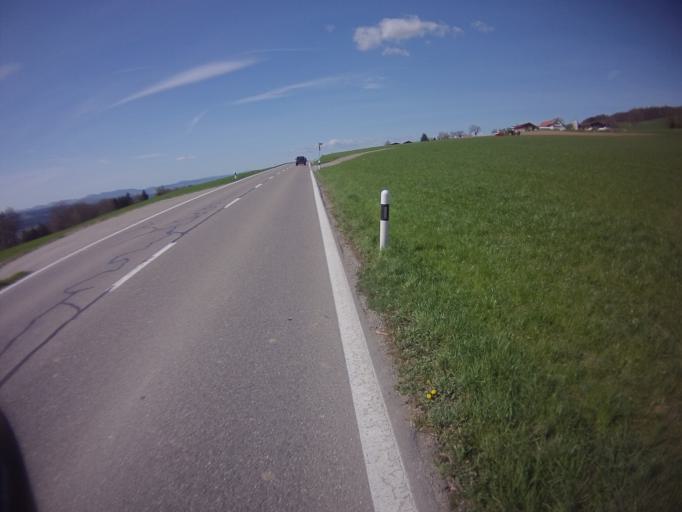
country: CH
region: Aargau
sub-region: Bezirk Baden
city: Kunten
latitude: 47.3793
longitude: 8.3522
